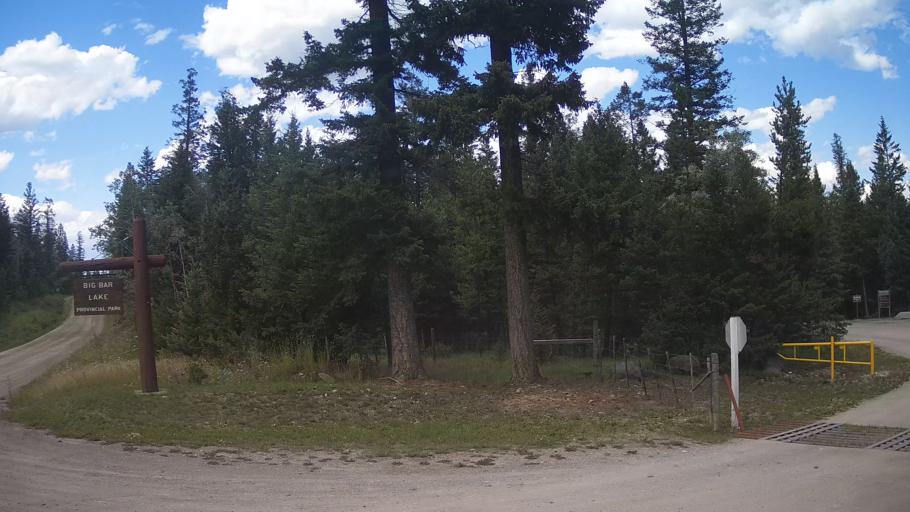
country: CA
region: British Columbia
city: Lillooet
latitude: 51.3090
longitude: -121.8234
